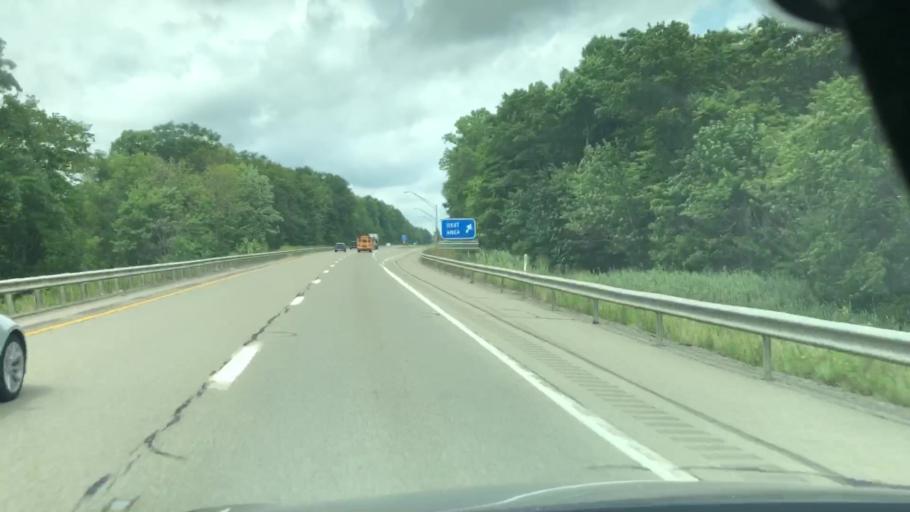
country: US
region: Pennsylvania
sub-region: Erie County
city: Edinboro
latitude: 41.8372
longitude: -80.1759
